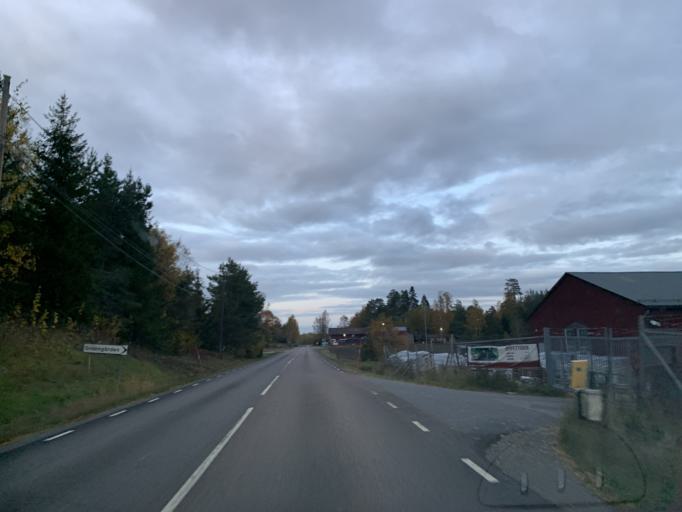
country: SE
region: Stockholm
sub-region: Nynashamns Kommun
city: Osmo
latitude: 58.9941
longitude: 17.7967
